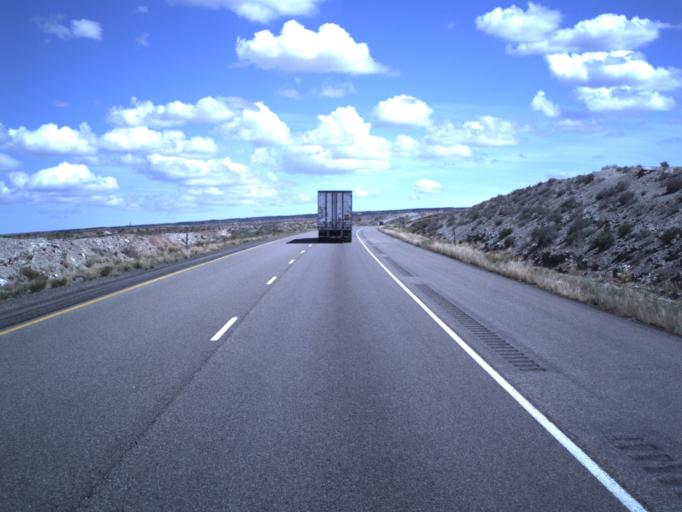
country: US
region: Utah
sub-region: Emery County
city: Ferron
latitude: 38.8474
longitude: -111.0122
